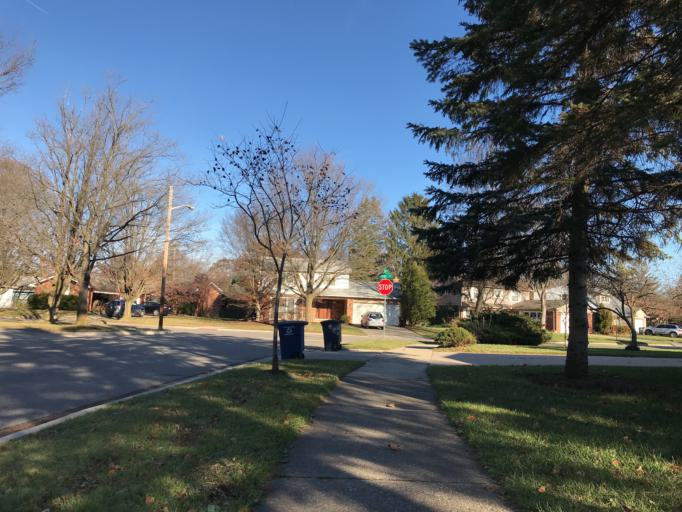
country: US
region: Michigan
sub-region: Washtenaw County
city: Ann Arbor
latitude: 42.2512
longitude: -83.7284
